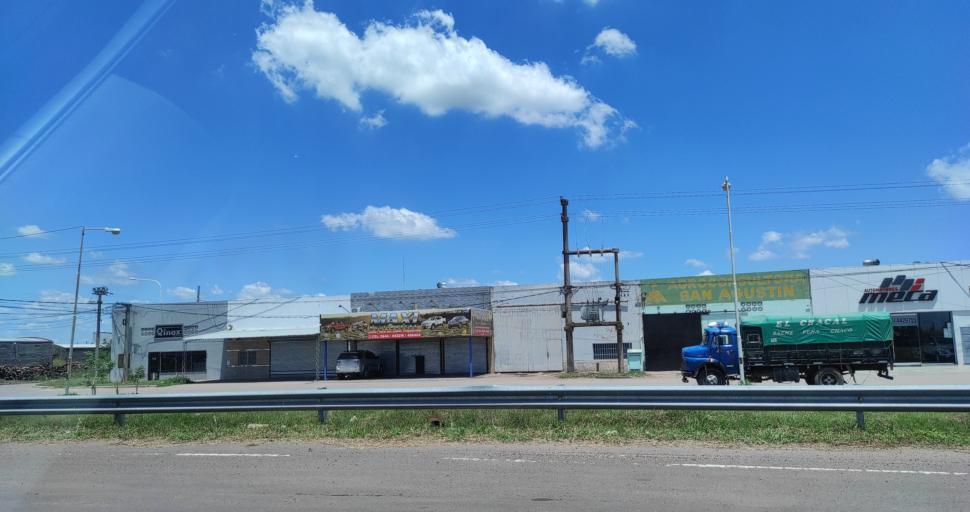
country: AR
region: Chaco
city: Presidencia Roque Saenz Pena
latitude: -26.8025
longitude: -60.4531
